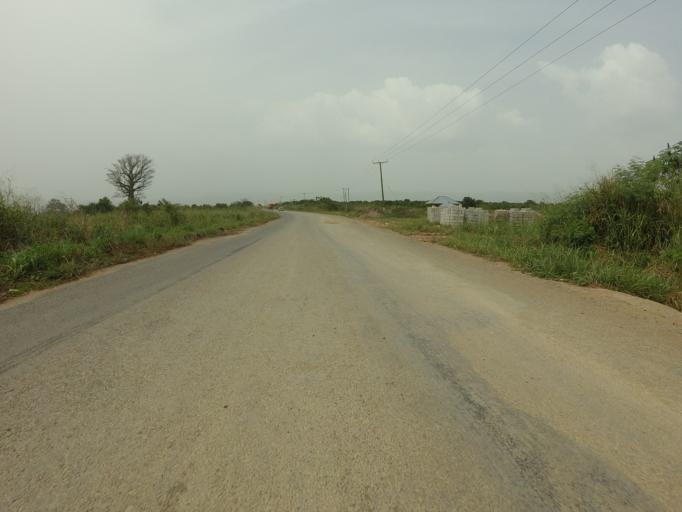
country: GH
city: Akropong
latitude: 6.0975
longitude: 0.0305
